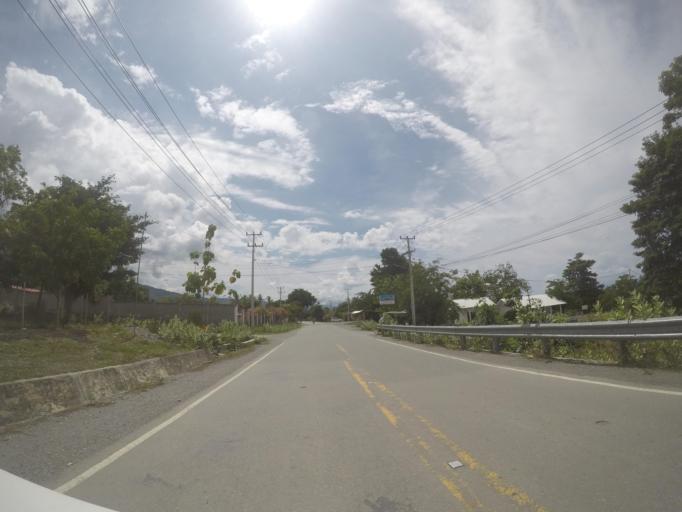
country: TL
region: Liquica
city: Liquica
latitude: -8.5851
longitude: 125.3522
